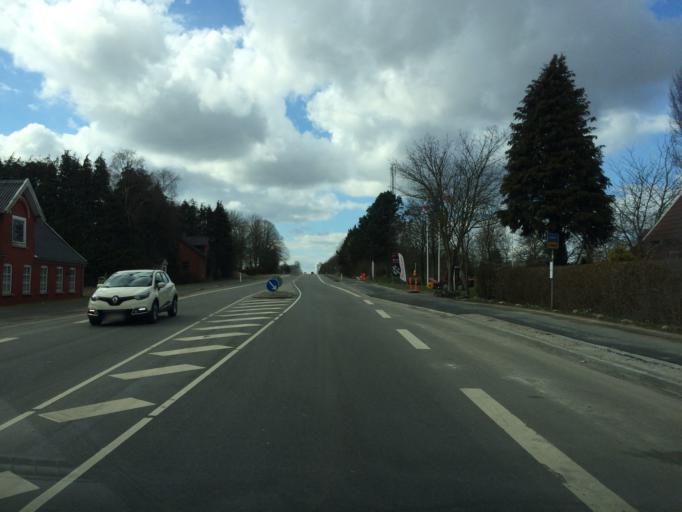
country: DK
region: South Denmark
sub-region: Assens Kommune
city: Tommerup Stationsby
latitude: 55.3873
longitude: 10.1878
